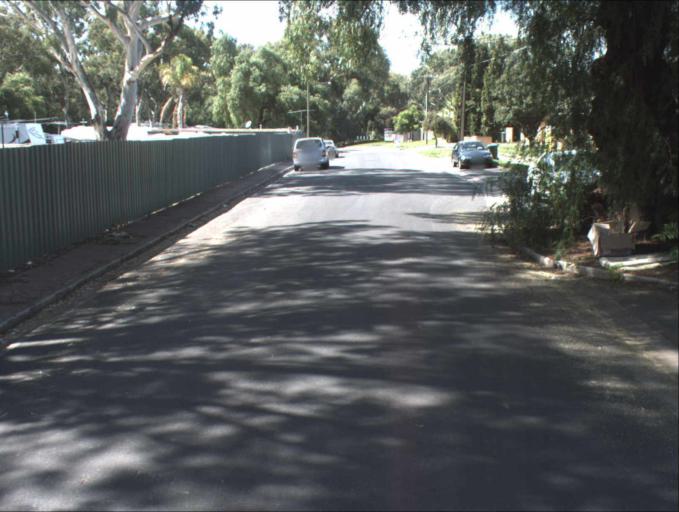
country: AU
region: South Australia
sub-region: Port Adelaide Enfield
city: Klemzig
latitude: -34.8788
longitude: 138.6475
